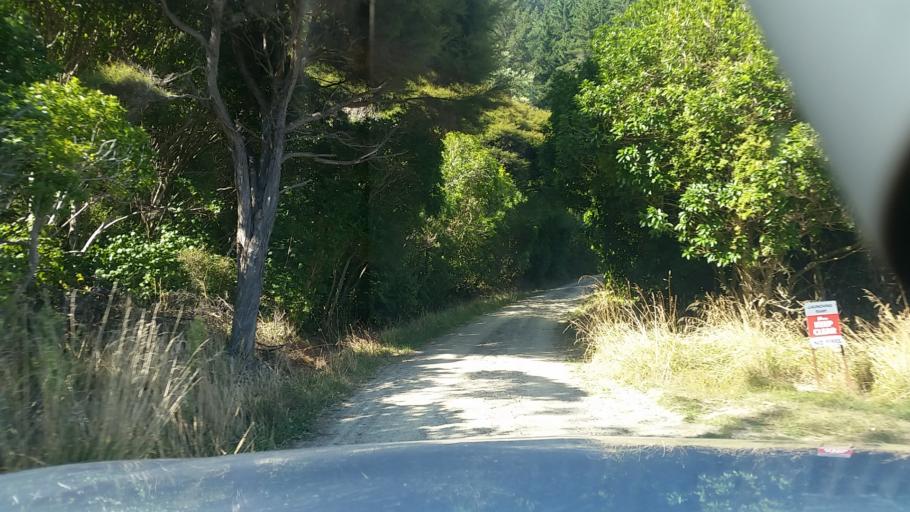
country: NZ
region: Marlborough
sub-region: Marlborough District
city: Picton
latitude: -41.3039
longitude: 174.1777
